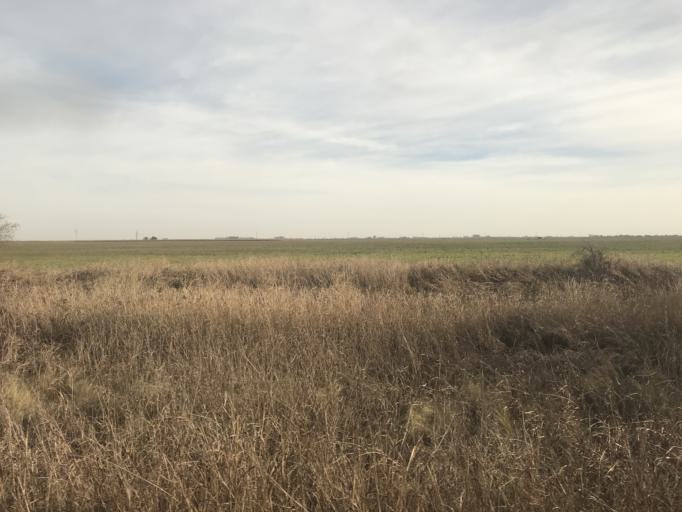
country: AR
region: Cordoba
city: Pilar
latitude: -31.6963
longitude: -63.8734
